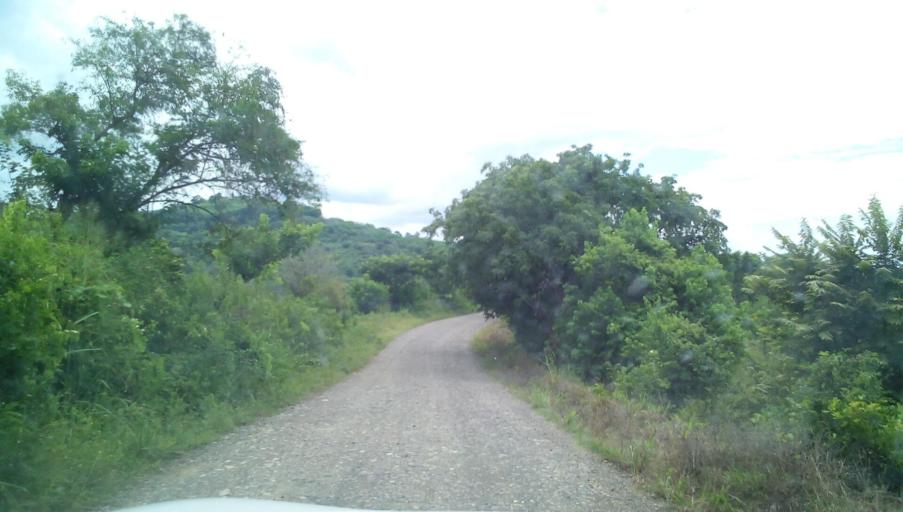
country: MX
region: Veracruz
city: Tepetzintla
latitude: 21.1470
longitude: -97.8563
